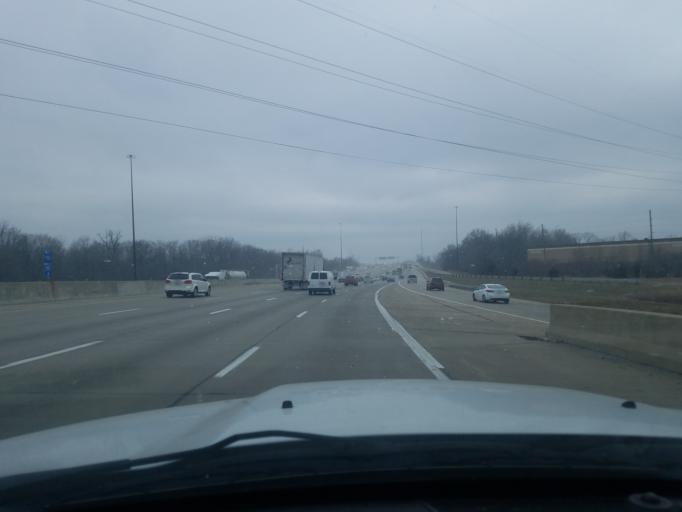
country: US
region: Indiana
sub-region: Marion County
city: Warren Park
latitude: 39.7998
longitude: -86.0483
